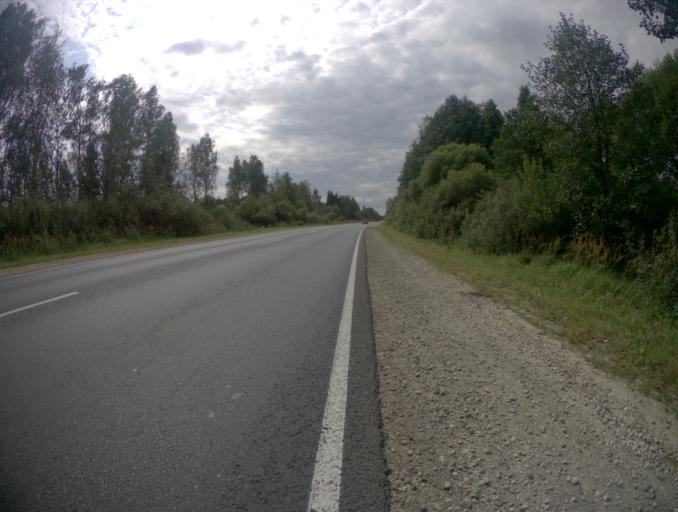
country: RU
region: Vladimir
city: Golovino
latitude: 56.0074
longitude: 40.5700
